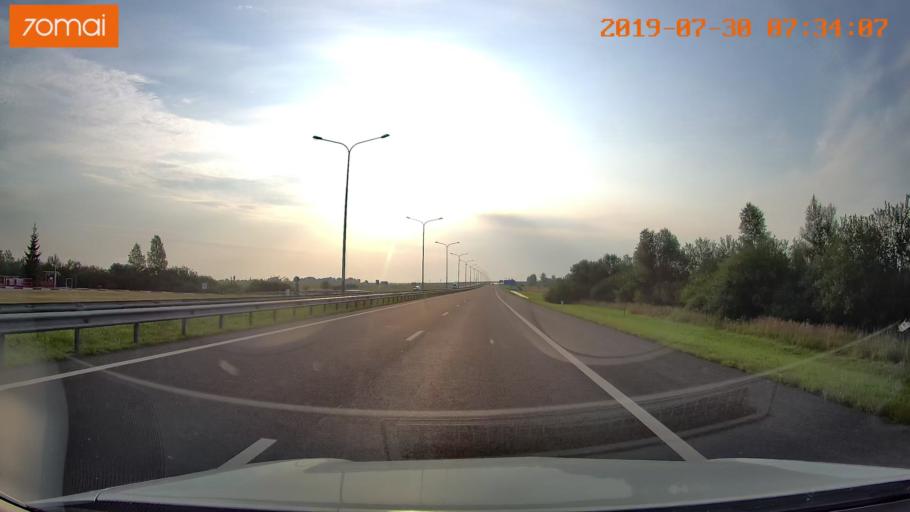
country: RU
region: Kaliningrad
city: Gvardeysk
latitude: 54.6718
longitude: 21.0638
